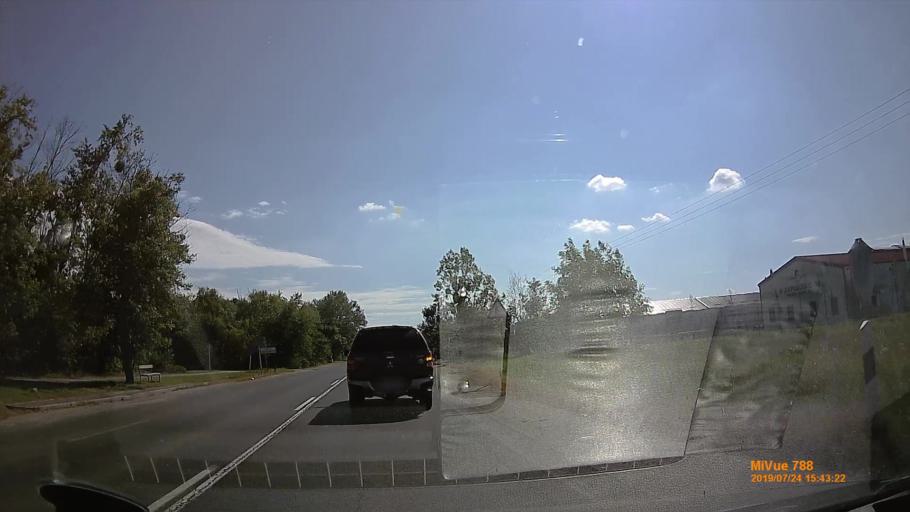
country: HU
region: Szabolcs-Szatmar-Bereg
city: Vasarosnameny
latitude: 48.1107
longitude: 22.3063
